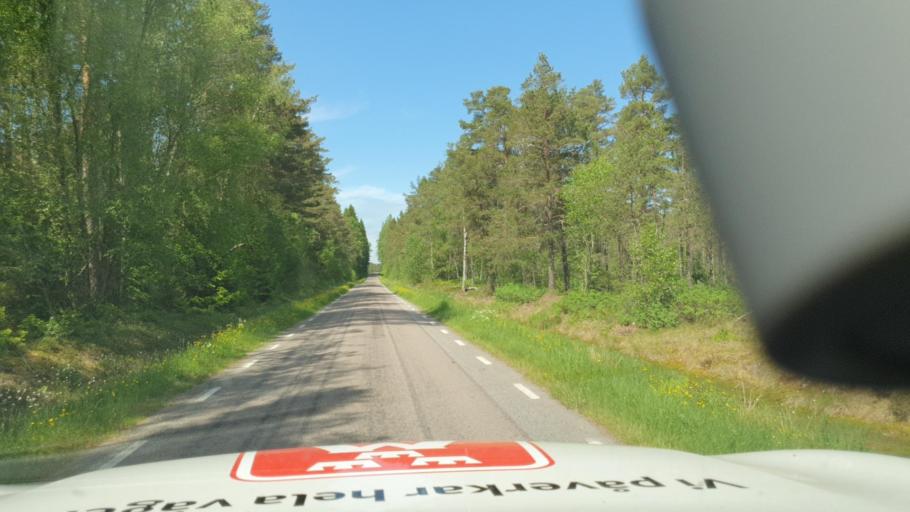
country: SE
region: Vaestra Goetaland
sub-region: Herrljunga Kommun
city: Herrljunga
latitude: 58.1216
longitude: 13.0996
